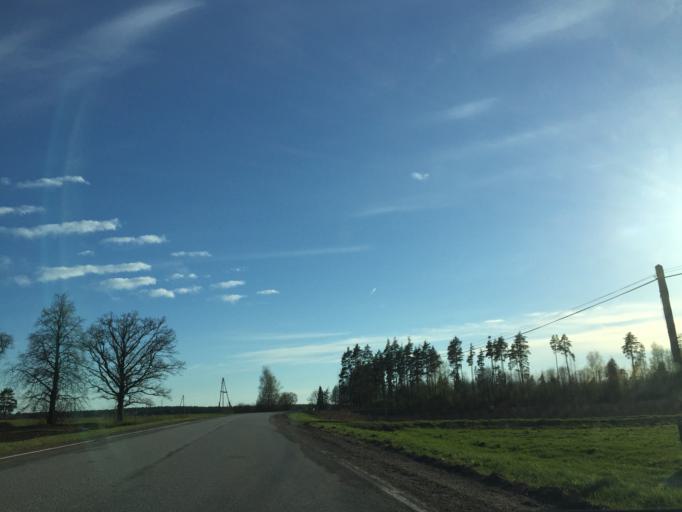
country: LV
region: Valkas Rajons
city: Valka
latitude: 57.7476
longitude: 25.9607
